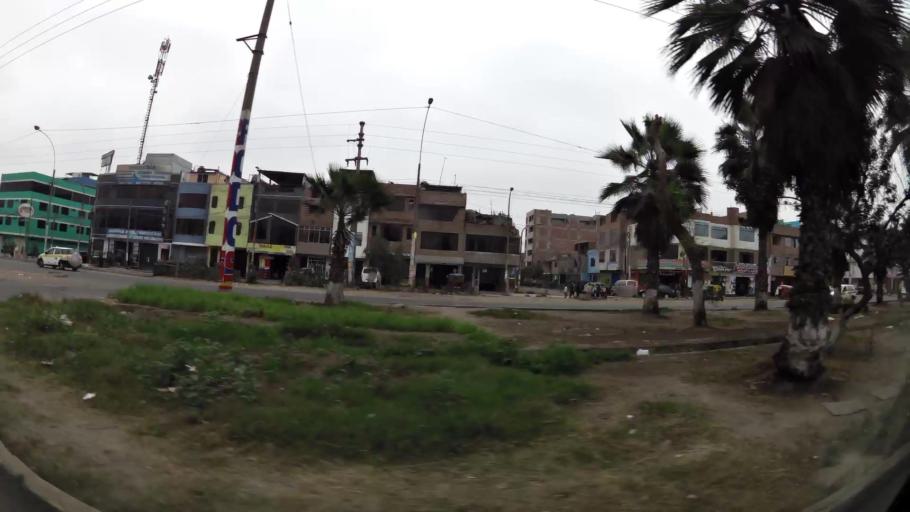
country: PE
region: Lima
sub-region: Lima
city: Urb. Santo Domingo
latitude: -11.9290
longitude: -77.0529
